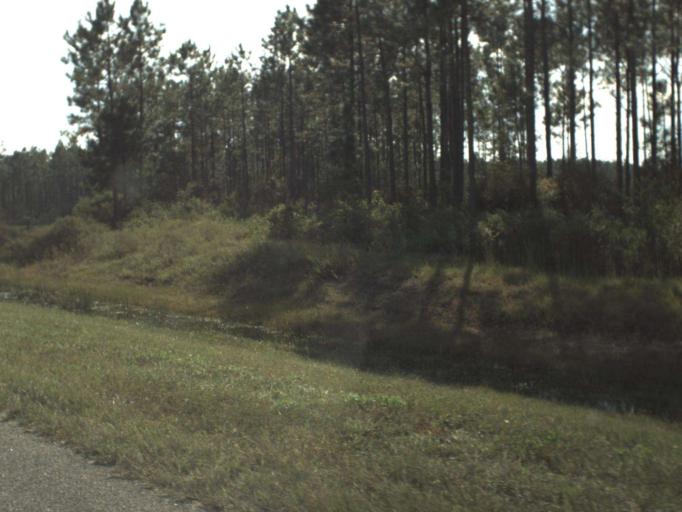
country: US
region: Florida
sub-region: Bay County
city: Laguna Beach
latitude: 30.3587
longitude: -85.8590
